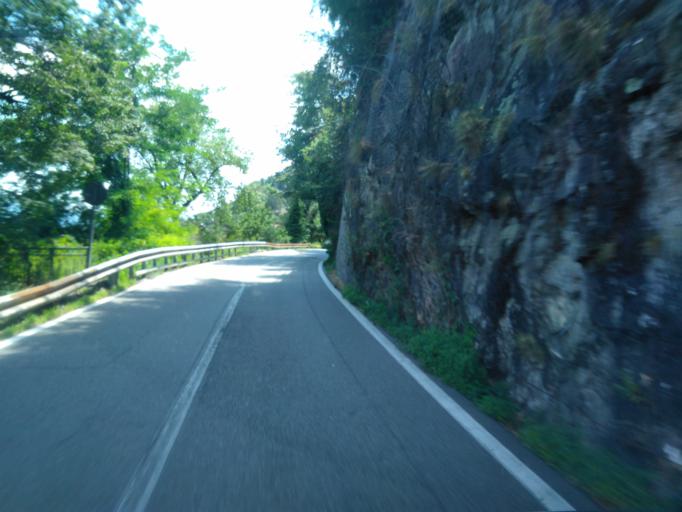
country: IT
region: Piedmont
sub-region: Provincia Verbano-Cusio-Ossola
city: Cannobio
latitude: 46.0811
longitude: 8.6928
